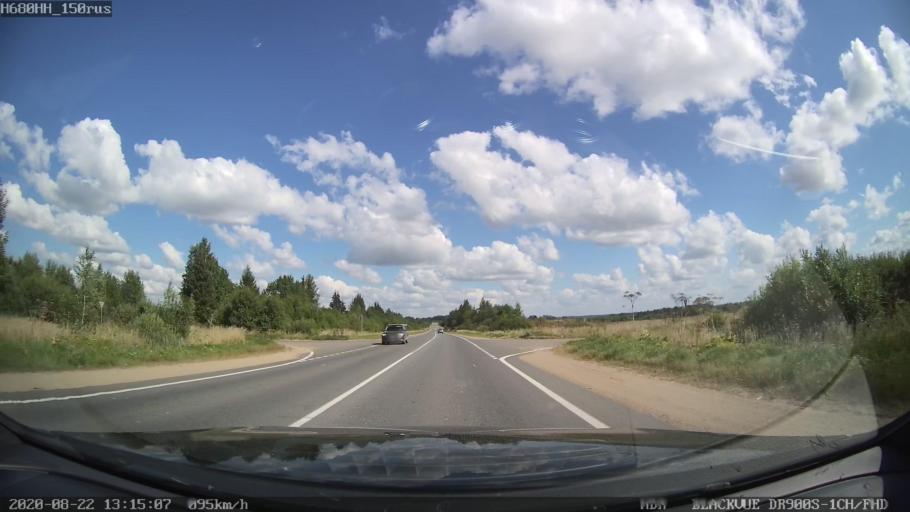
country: RU
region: Tverskaya
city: Bezhetsk
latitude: 57.7561
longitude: 36.6179
